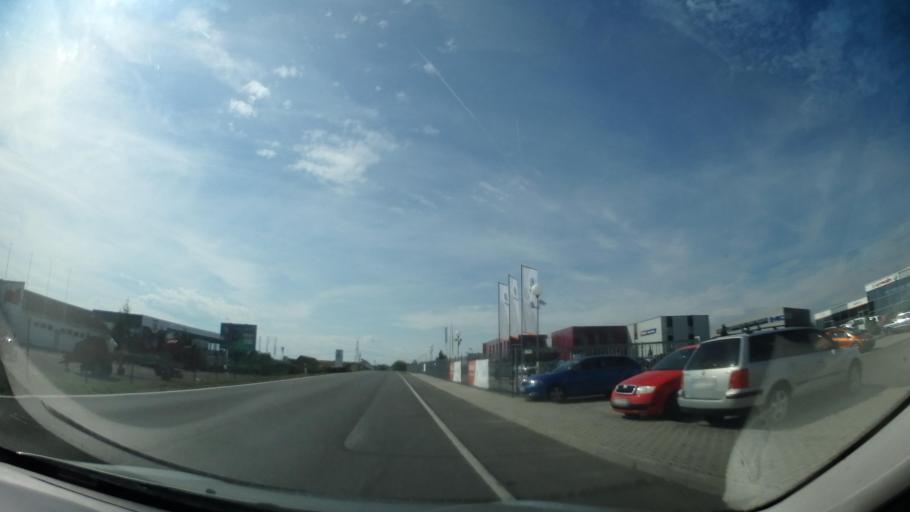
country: CZ
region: Jihocesky
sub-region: Okres Pisek
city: Pisek
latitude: 49.3074
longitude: 14.0970
